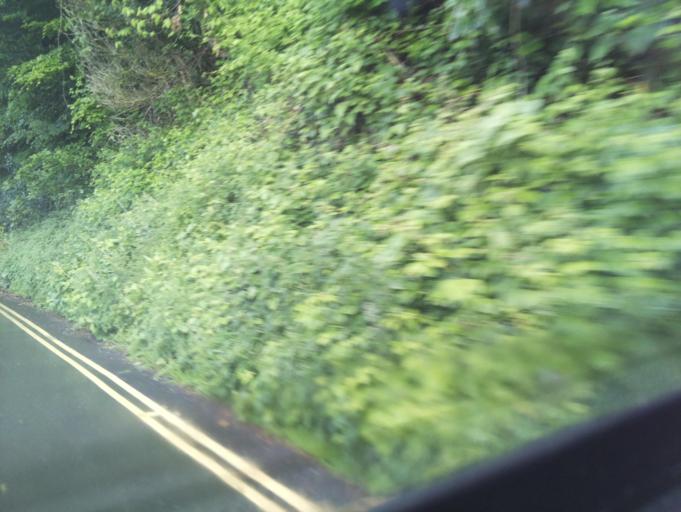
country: GB
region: England
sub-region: Devon
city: Dartmouth
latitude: 50.3496
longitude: -3.5677
